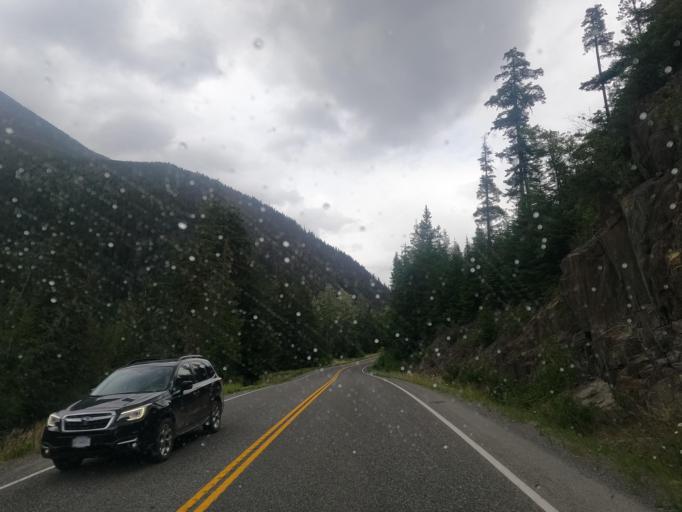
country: CA
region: British Columbia
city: Lillooet
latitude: 50.4888
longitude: -122.2029
